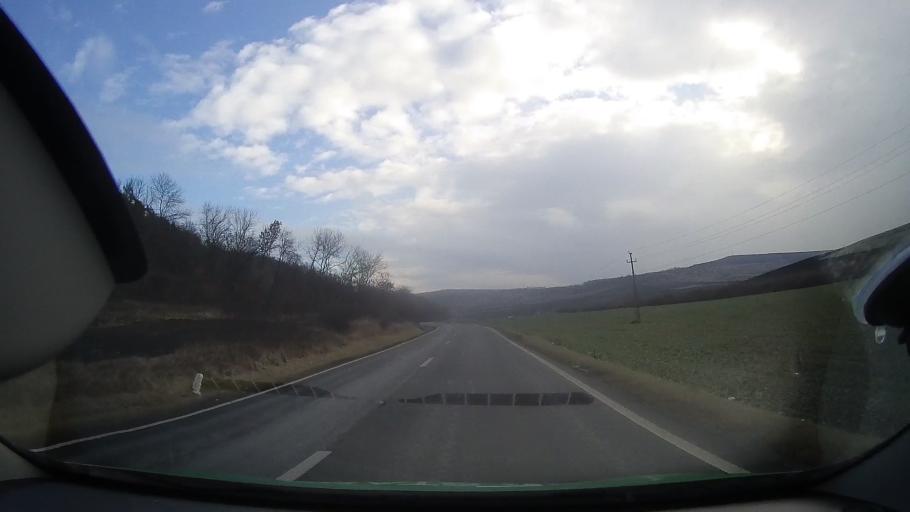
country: RO
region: Mures
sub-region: Comuna Cucerdea
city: Cucerdea
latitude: 46.3689
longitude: 24.2628
